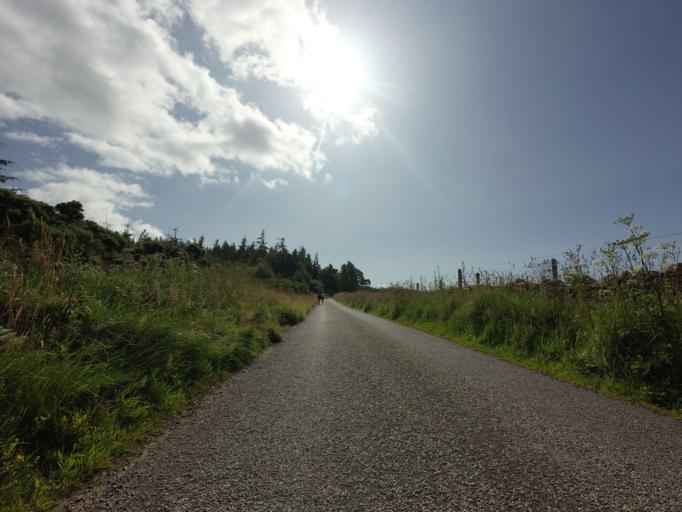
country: GB
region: Scotland
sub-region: Highland
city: Nairn
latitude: 57.5314
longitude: -3.8635
